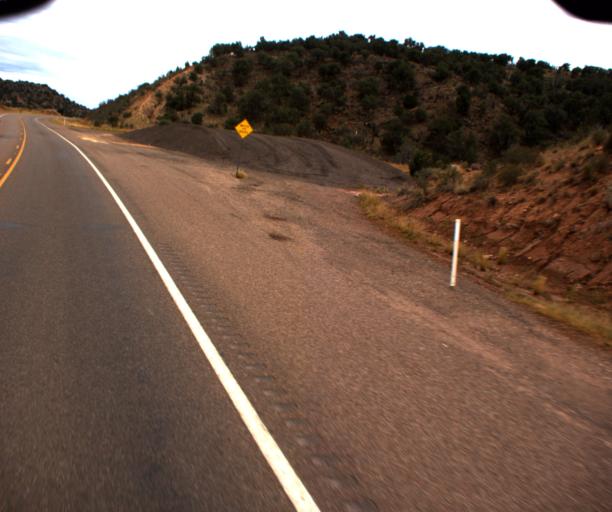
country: US
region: Arizona
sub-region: Navajo County
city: Taylor
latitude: 34.4010
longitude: -110.0719
